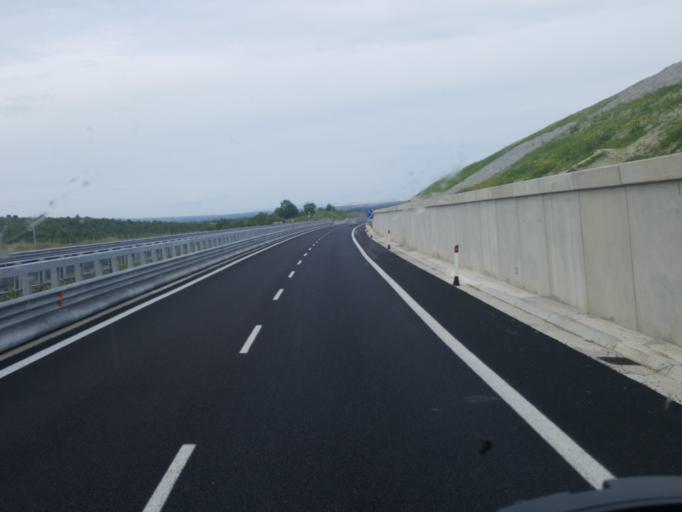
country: IT
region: Latium
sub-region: Provincia di Viterbo
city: Monte Romano
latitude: 42.2920
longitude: 11.9415
